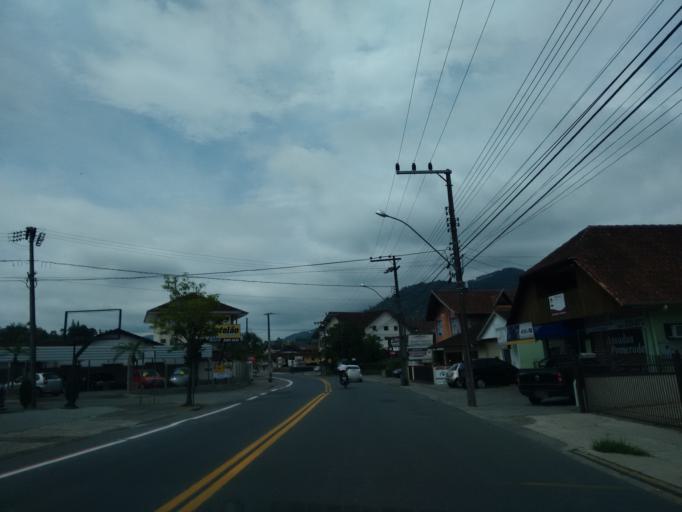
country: BR
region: Santa Catarina
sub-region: Pomerode
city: Pomerode
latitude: -26.7239
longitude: -49.1698
